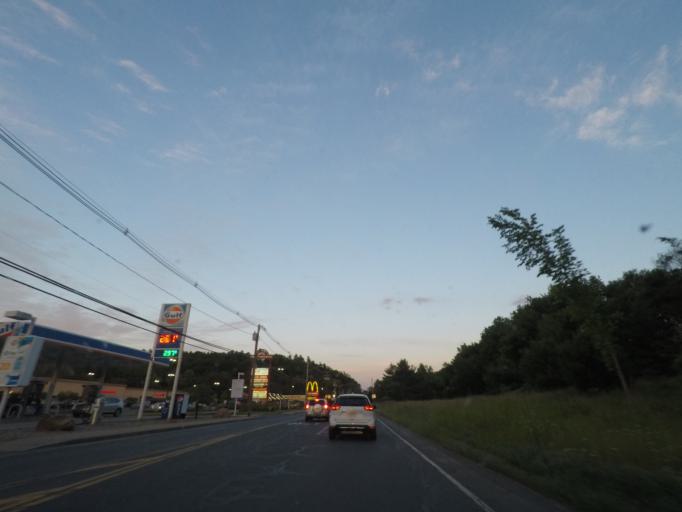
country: US
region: Massachusetts
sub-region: Worcester County
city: Southbridge
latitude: 42.0692
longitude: -72.0107
